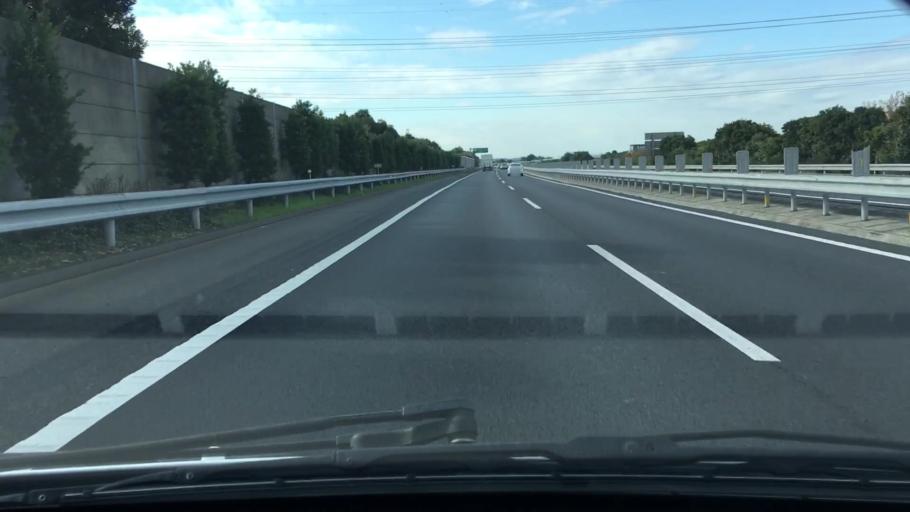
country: JP
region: Chiba
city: Ichihara
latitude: 35.5102
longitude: 140.1112
